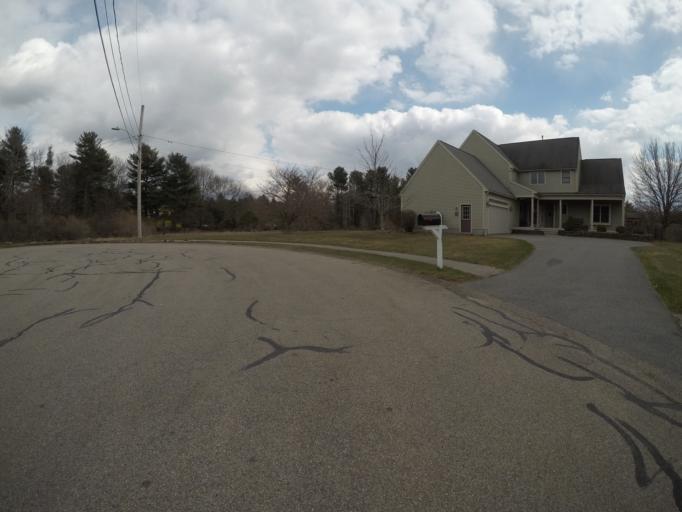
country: US
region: Massachusetts
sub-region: Bristol County
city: Easton
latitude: 42.0545
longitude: -71.1322
